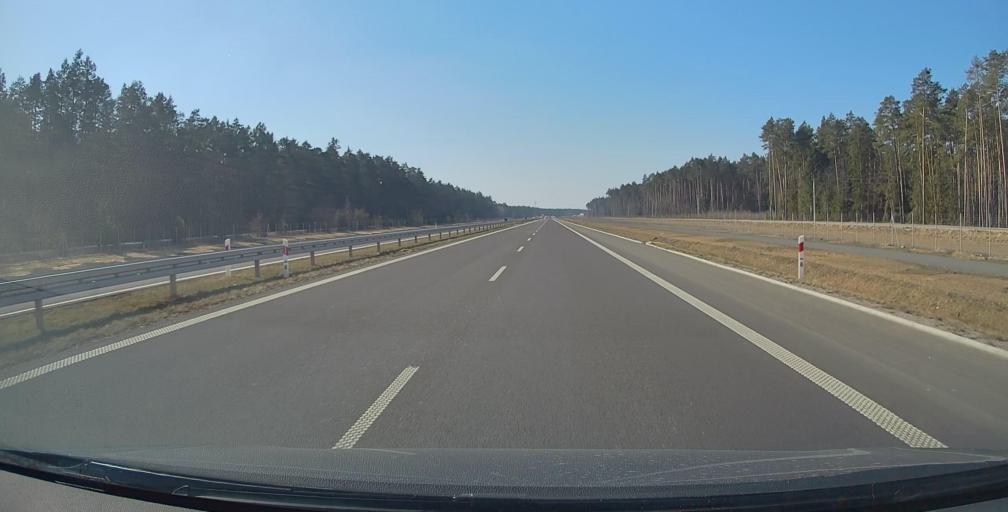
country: PL
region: Lublin Voivodeship
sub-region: Powiat janowski
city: Modliborzyce
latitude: 50.6670
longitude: 22.3225
